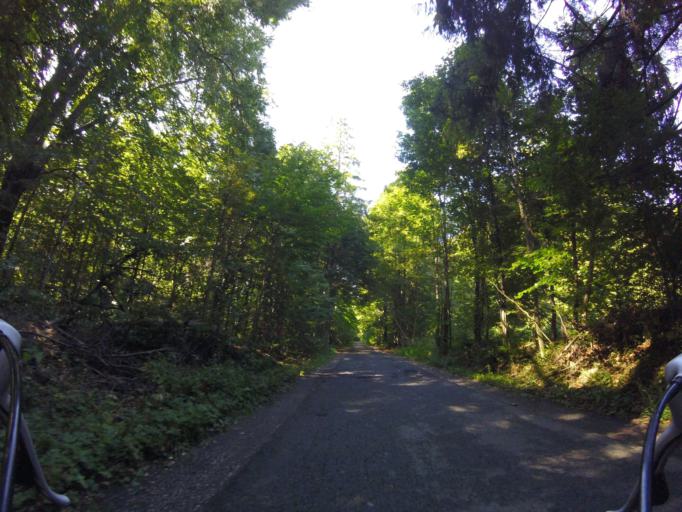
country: HU
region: Heves
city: Szilvasvarad
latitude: 48.1047
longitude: 20.5618
